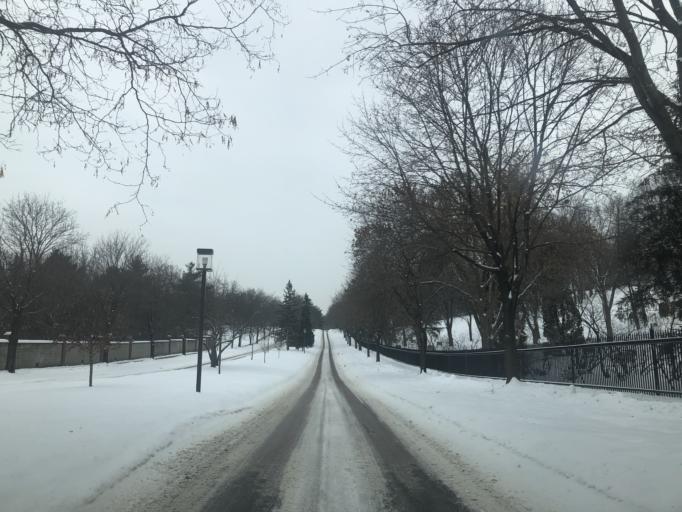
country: US
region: Minnesota
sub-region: Hennepin County
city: Richfield
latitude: 44.9327
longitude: -93.2935
